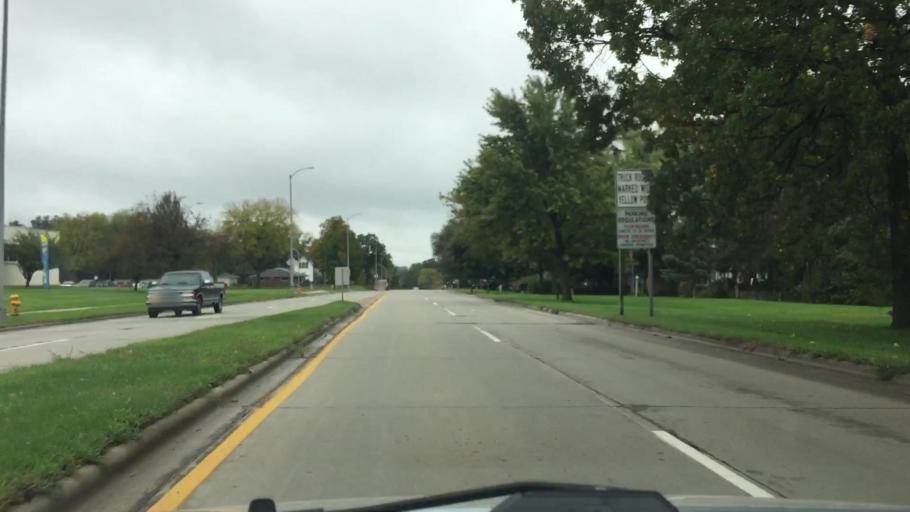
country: US
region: Wisconsin
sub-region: Rock County
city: Janesville
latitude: 42.7030
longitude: -89.0310
